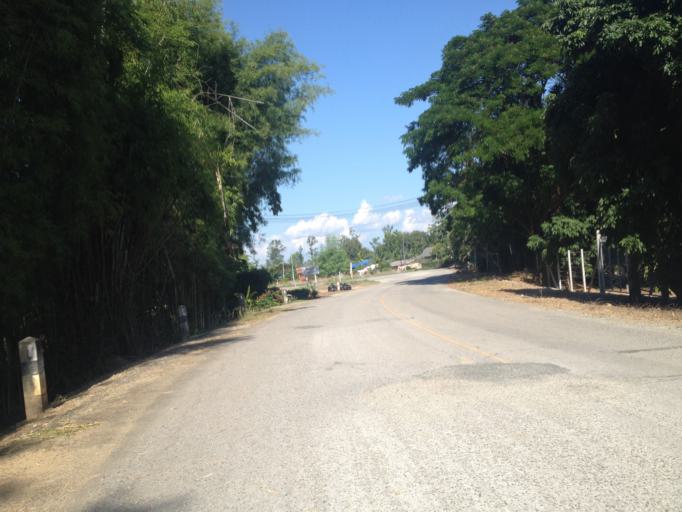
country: TH
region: Chiang Mai
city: Saraphi
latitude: 18.6849
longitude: 98.9877
